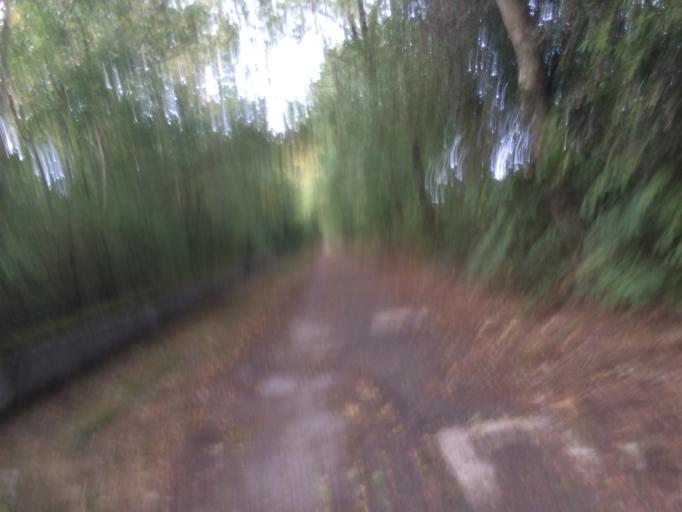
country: FR
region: Ile-de-France
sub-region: Departement de l'Essonne
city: Limours
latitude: 48.6584
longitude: 2.0885
